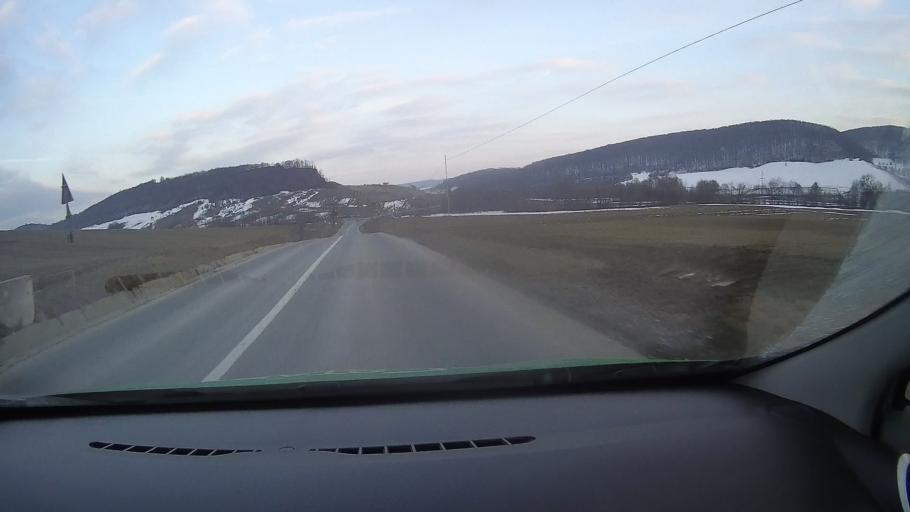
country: RO
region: Harghita
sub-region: Comuna Lupeni
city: Lupeni
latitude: 46.3612
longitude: 25.1841
